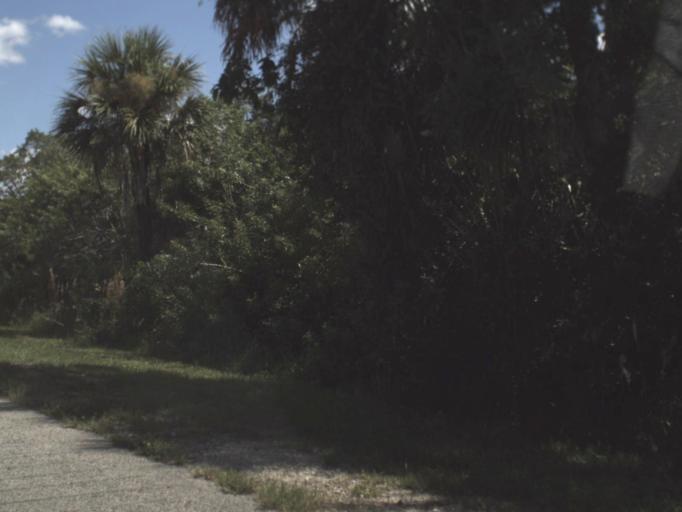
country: US
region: Florida
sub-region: Collier County
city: Marco
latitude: 25.9605
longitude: -81.4996
